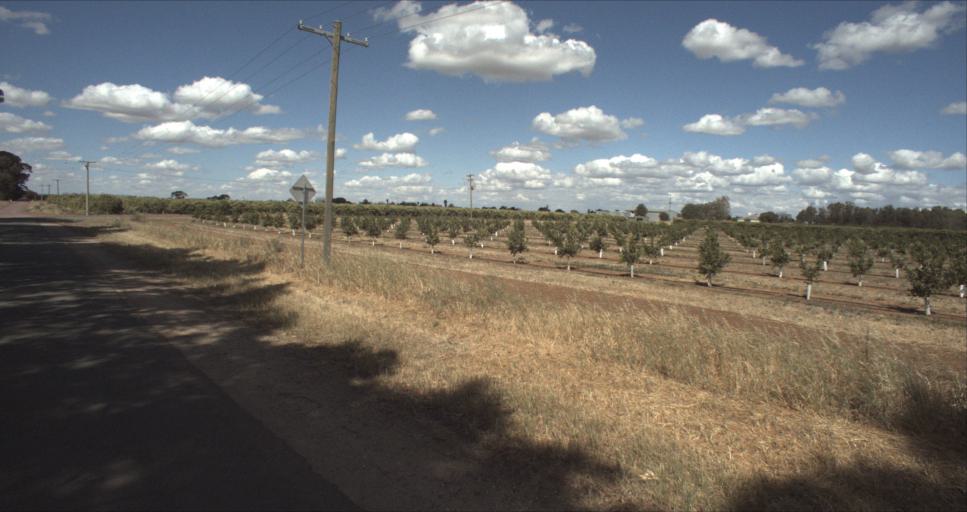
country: AU
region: New South Wales
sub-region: Leeton
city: Leeton
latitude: -34.5095
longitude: 146.2306
